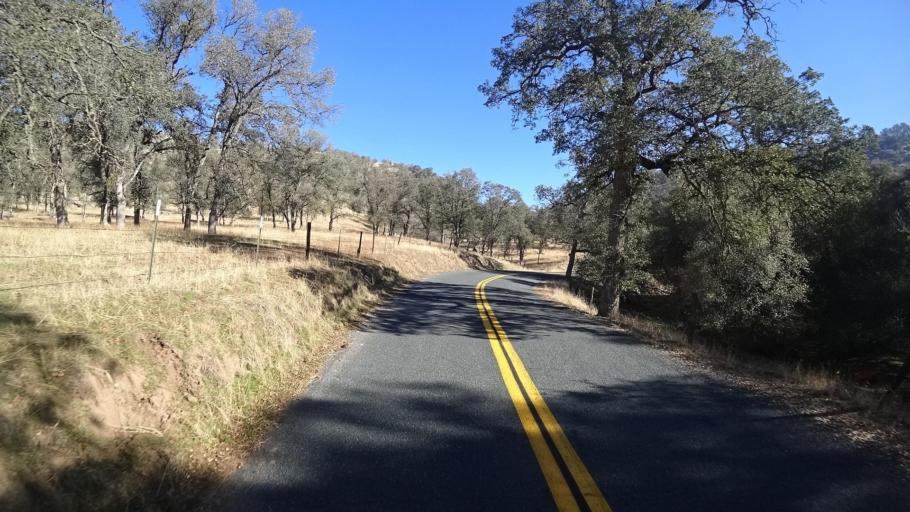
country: US
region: California
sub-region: Kern County
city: Alta Sierra
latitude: 35.7861
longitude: -118.7744
